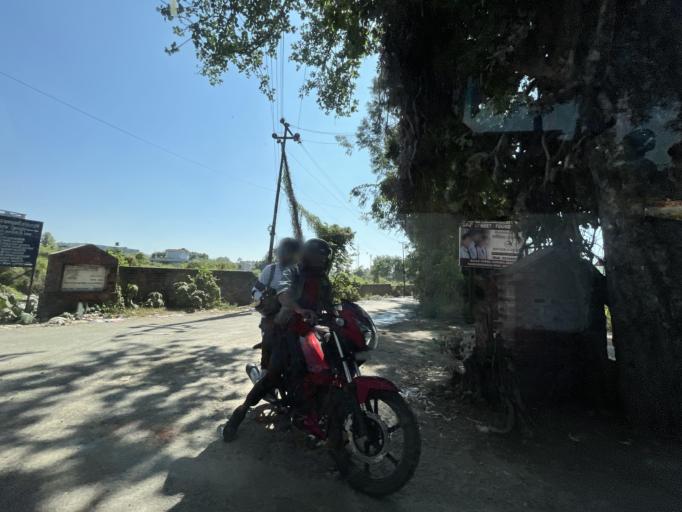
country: IN
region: Uttarakhand
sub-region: Naini Tal
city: Haldwani
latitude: 29.2129
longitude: 79.4744
